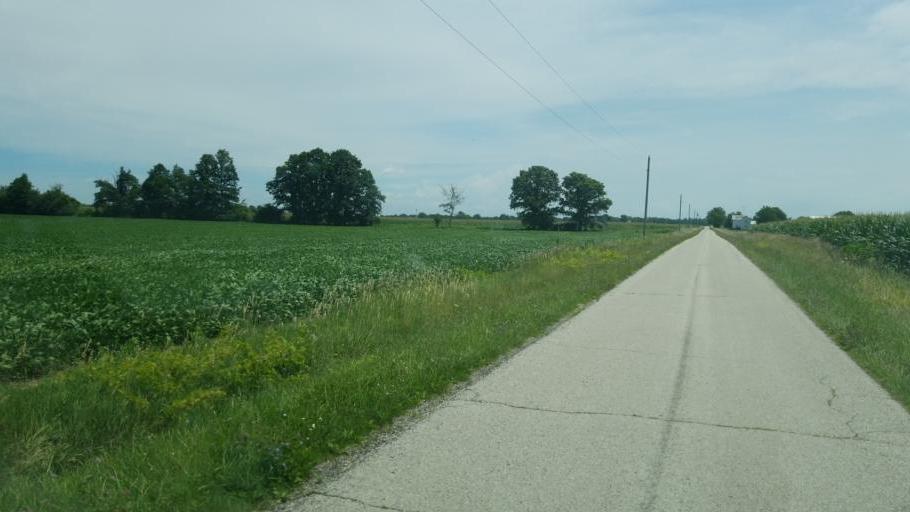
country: US
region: Ohio
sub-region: Crawford County
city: Bucyrus
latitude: 40.8776
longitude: -82.9754
